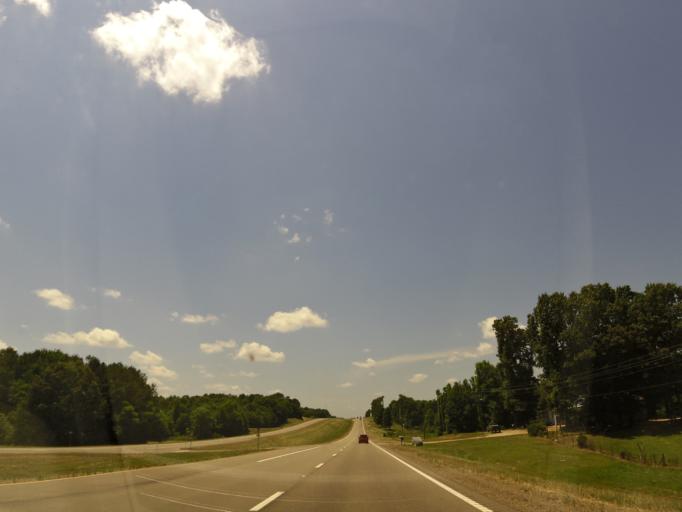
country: US
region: Mississippi
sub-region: Pontotoc County
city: Pontotoc
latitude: 34.2980
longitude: -89.2359
